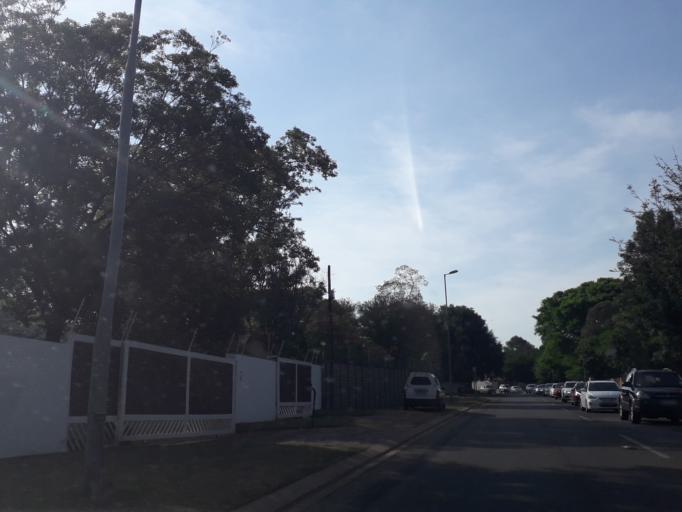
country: ZA
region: Gauteng
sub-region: City of Johannesburg Metropolitan Municipality
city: Diepsloot
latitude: -26.0334
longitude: 28.0161
